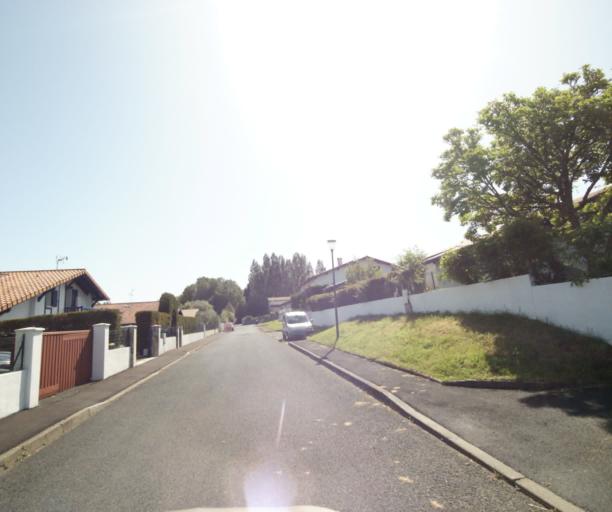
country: FR
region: Aquitaine
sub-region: Departement des Pyrenees-Atlantiques
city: Villefranque
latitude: 43.4581
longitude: -1.4525
